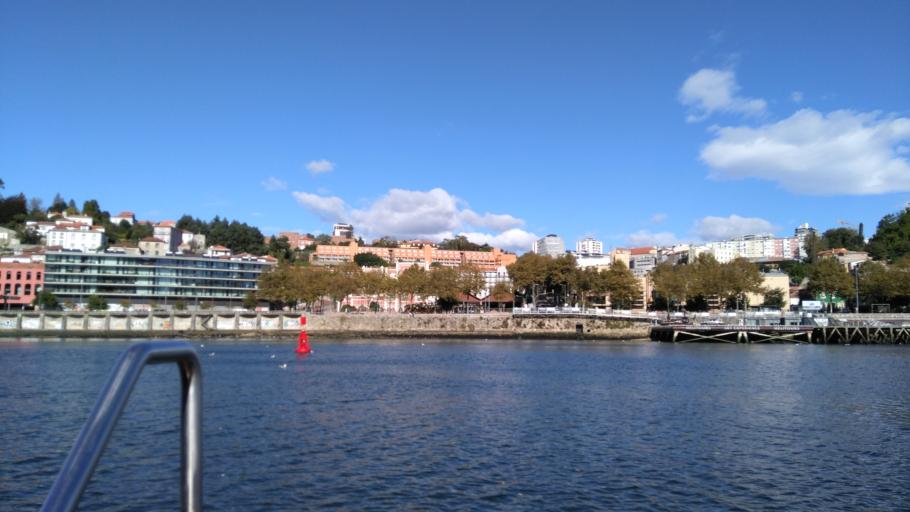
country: PT
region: Porto
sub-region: Vila Nova de Gaia
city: Vila Nova de Gaia
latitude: 41.1457
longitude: -8.6342
